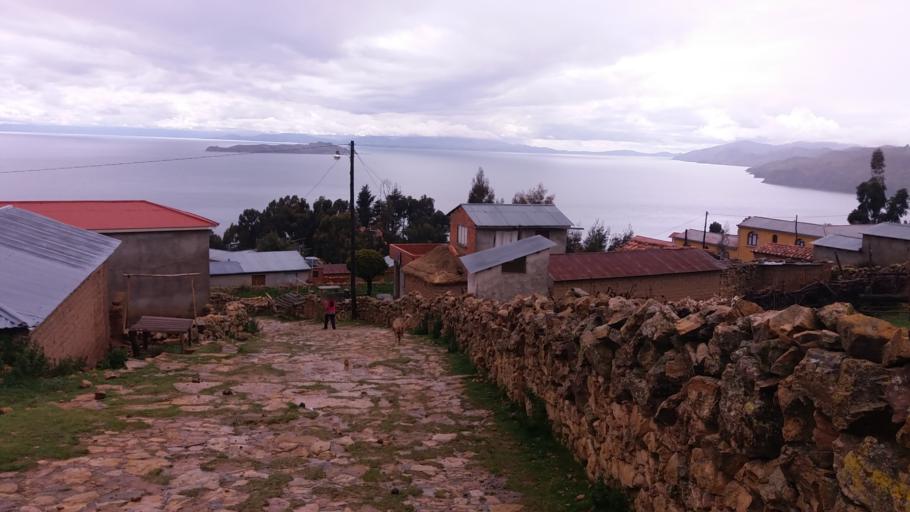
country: BO
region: La Paz
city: Yumani
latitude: -16.0361
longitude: -69.1487
